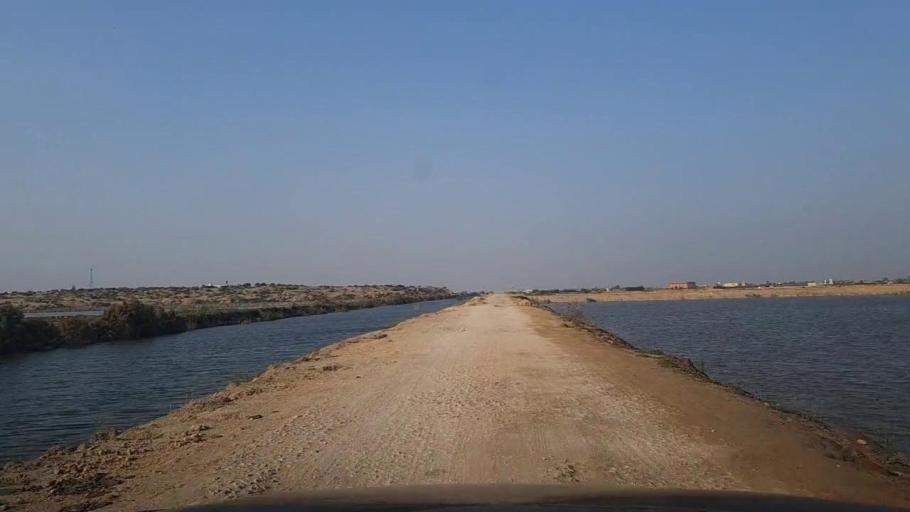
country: PK
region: Sindh
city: Thatta
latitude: 24.7369
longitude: 67.9064
